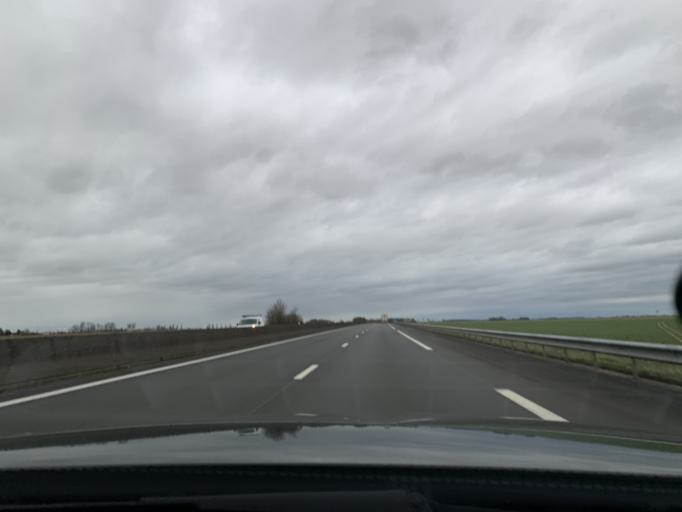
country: FR
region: Picardie
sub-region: Departement de l'Oise
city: Tille
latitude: 49.5067
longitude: 2.1776
